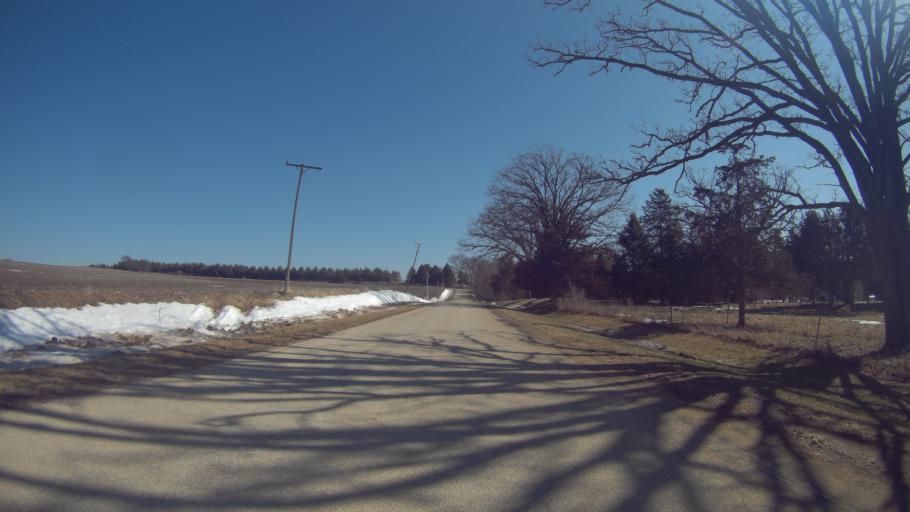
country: US
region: Illinois
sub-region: Winnebago County
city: Lake Summerset
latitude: 42.4293
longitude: -89.4412
